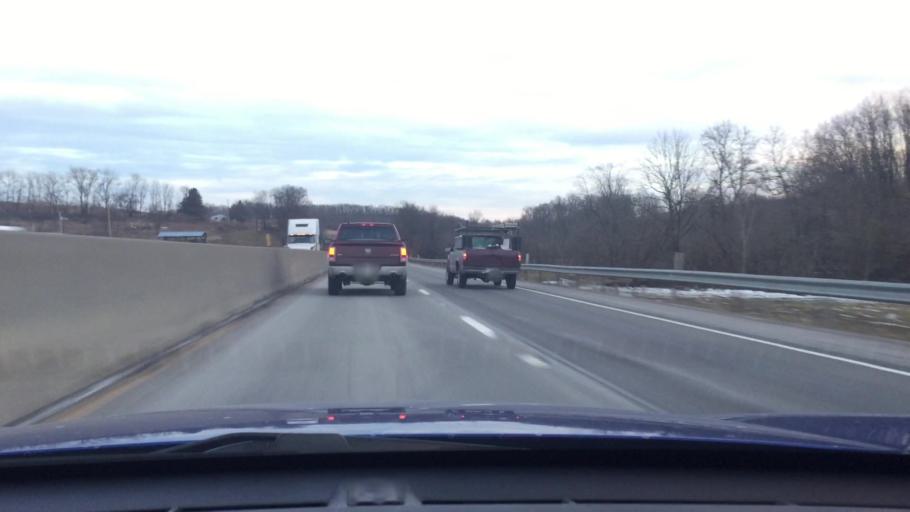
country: US
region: Pennsylvania
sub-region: Washington County
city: Ellsworth
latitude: 40.1564
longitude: -80.0437
